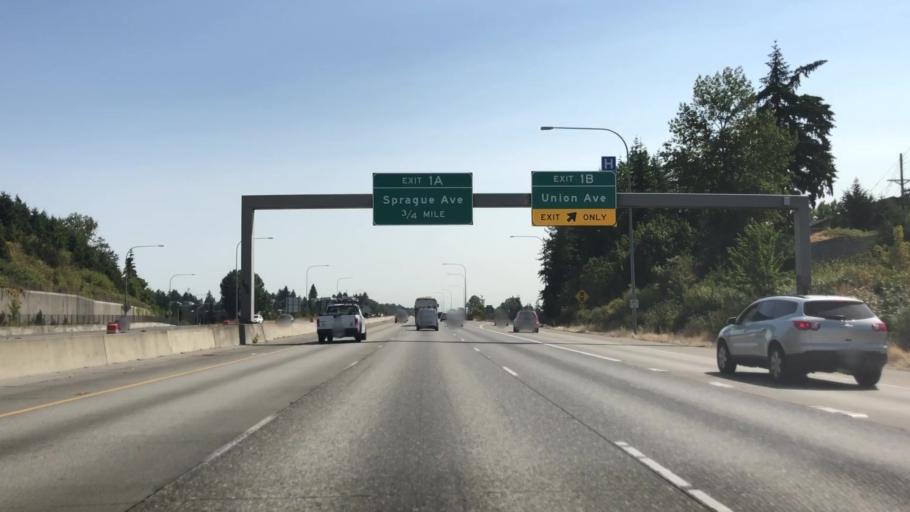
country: US
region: Washington
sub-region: Pierce County
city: Fircrest
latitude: 47.2347
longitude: -122.4872
